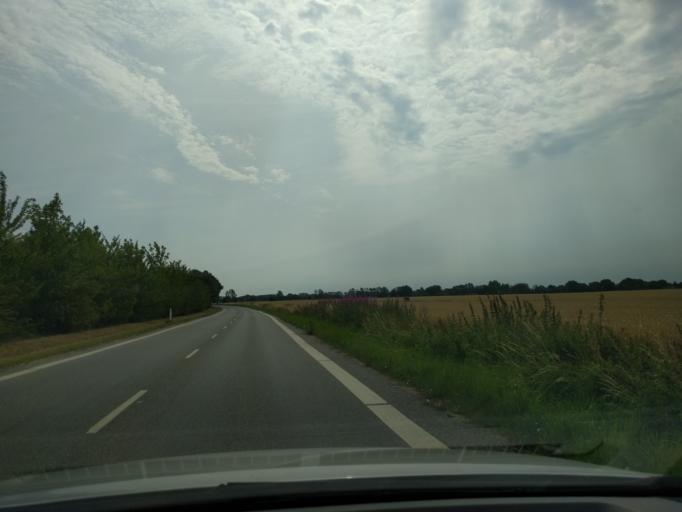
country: DK
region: South Denmark
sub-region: Nordfyns Kommune
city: Otterup
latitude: 55.5592
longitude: 10.4577
